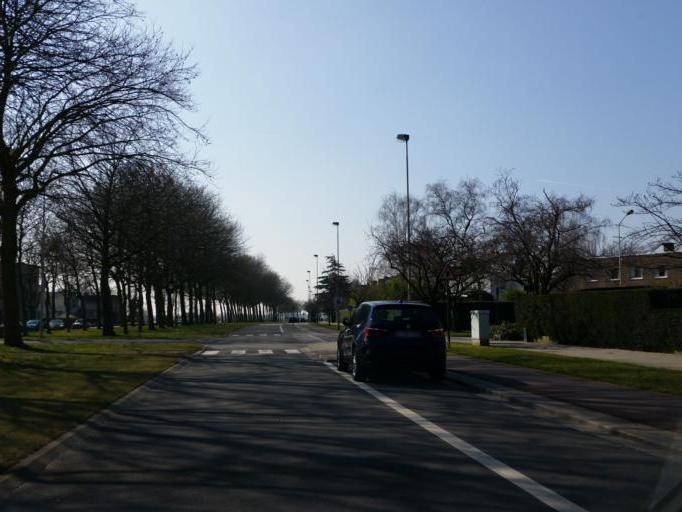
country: BE
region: Flanders
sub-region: Provincie Antwerpen
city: Antwerpen
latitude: 51.2170
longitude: 4.3845
